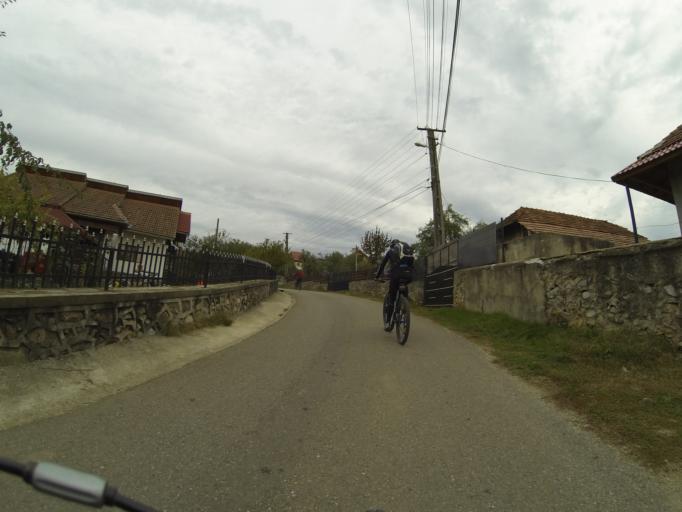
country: RO
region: Gorj
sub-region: Comuna Tismana
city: Sohodol
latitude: 45.0494
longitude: 22.8977
